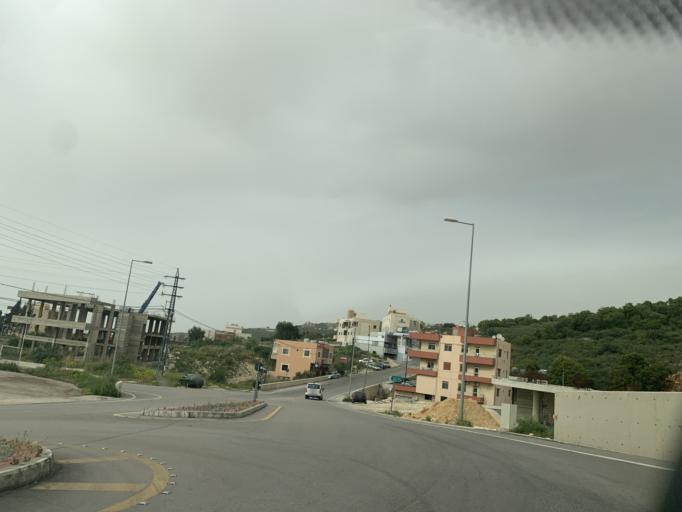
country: LB
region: Mont-Liban
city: Jbail
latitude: 34.1505
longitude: 35.6343
